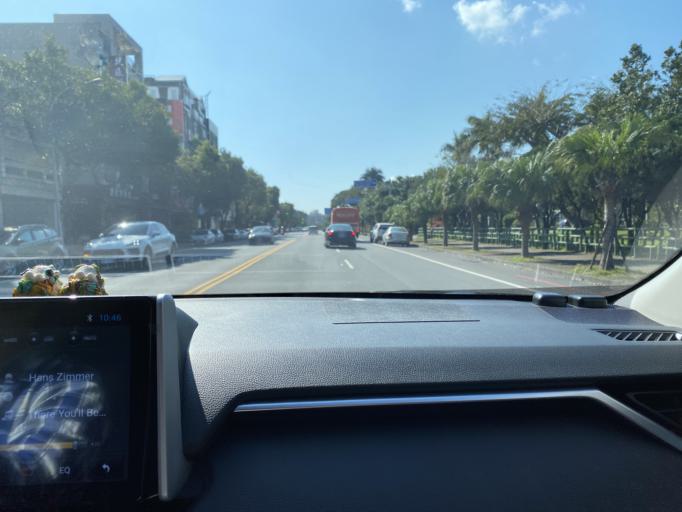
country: TW
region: Taiwan
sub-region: Hualien
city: Hualian
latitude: 23.9902
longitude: 121.6215
